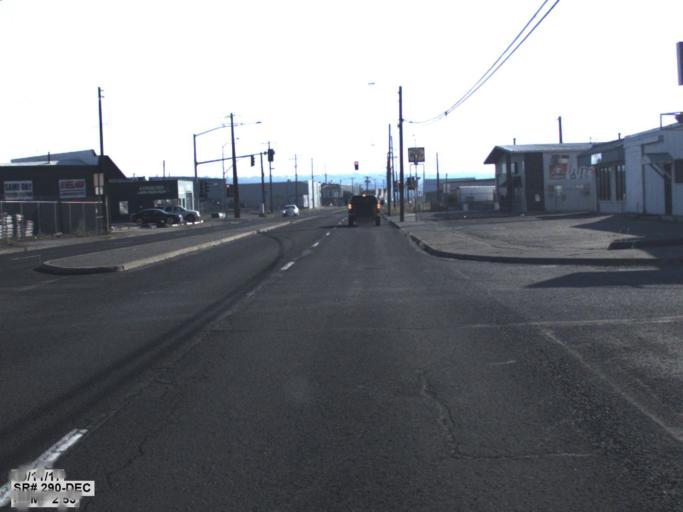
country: US
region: Washington
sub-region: Spokane County
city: Spokane
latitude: 47.6679
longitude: -117.3605
